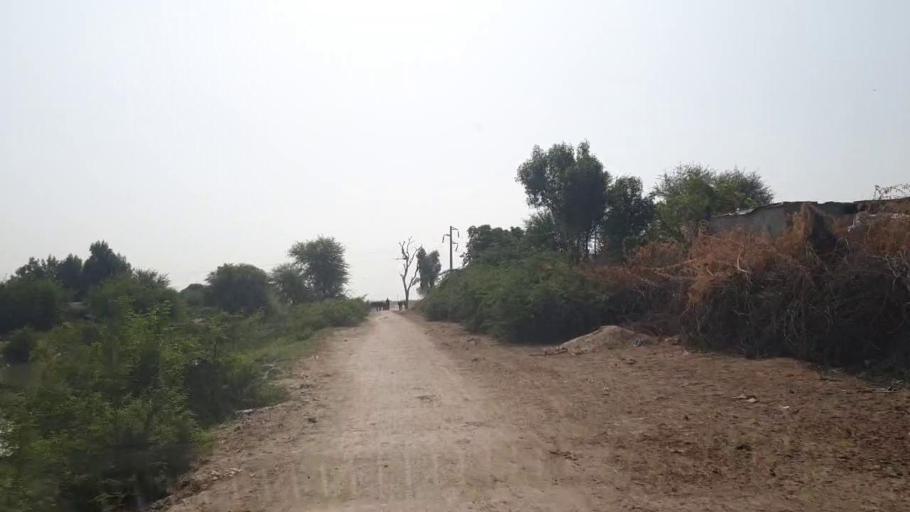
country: PK
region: Sindh
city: Badin
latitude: 24.6381
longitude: 68.8498
